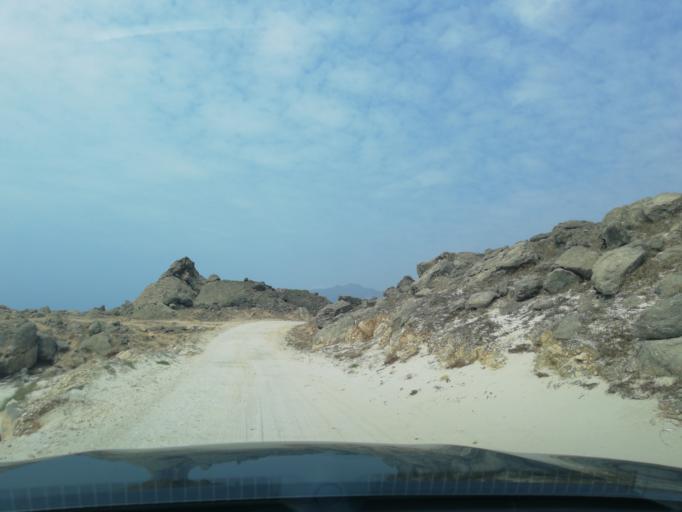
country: OM
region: Zufar
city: Salalah
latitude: 16.8348
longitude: 53.7157
